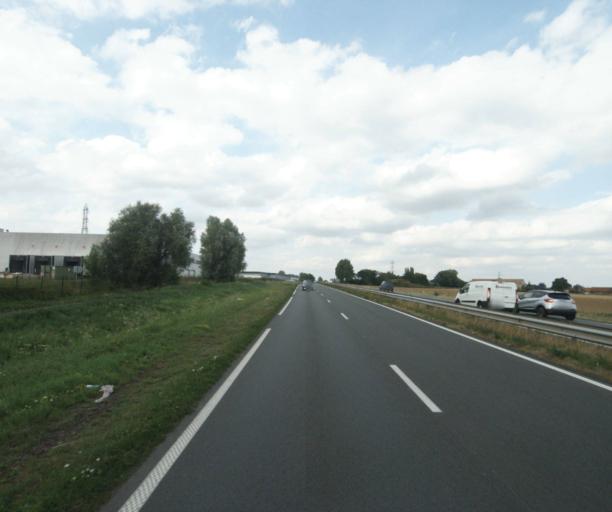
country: FR
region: Nord-Pas-de-Calais
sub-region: Departement du Nord
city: Sailly-lez-Lannoy
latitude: 50.6493
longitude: 3.2062
